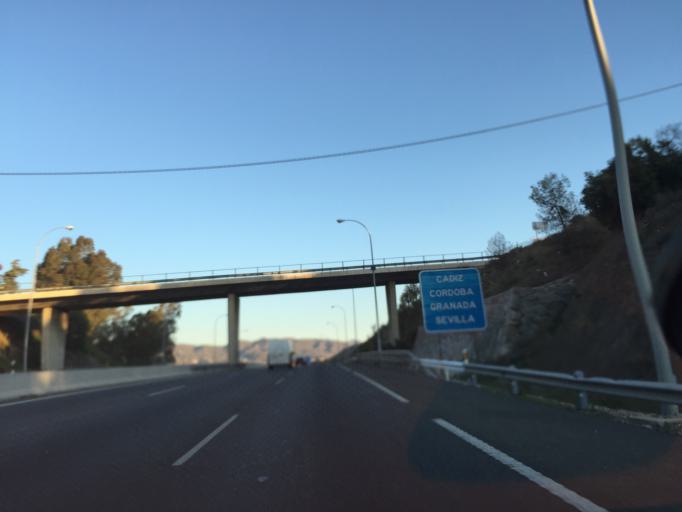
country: ES
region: Andalusia
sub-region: Provincia de Malaga
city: Malaga
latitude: 36.7455
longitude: -4.4078
